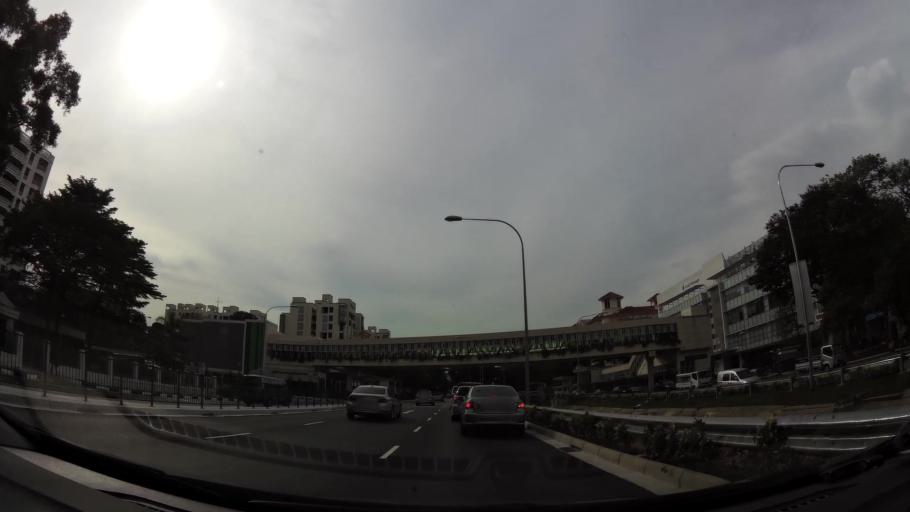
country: SG
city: Singapore
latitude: 1.3357
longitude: 103.7841
